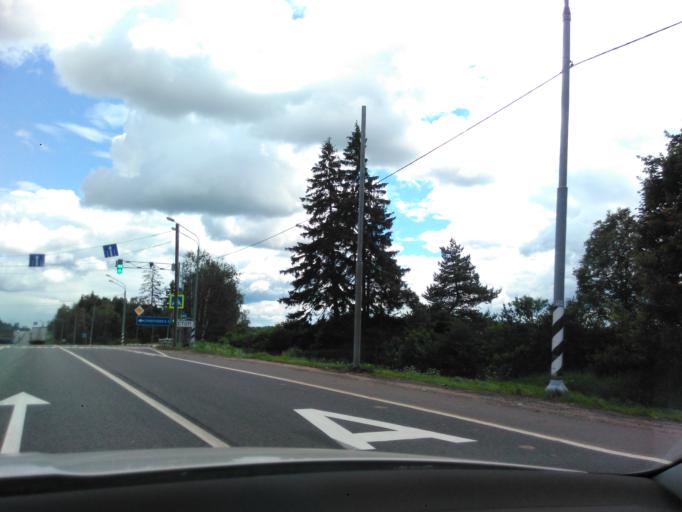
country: RU
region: Moskovskaya
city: Solnechnogorsk
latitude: 56.2196
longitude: 36.9258
